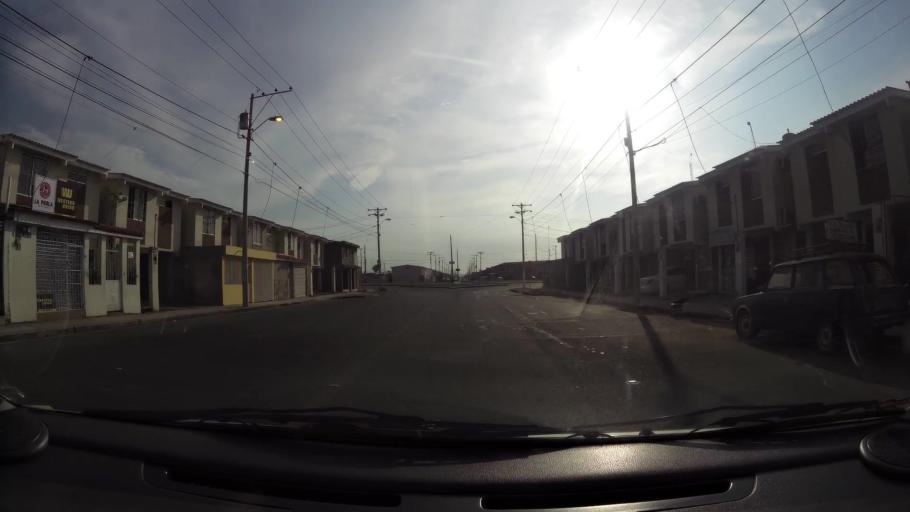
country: EC
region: Guayas
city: Eloy Alfaro
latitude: -2.0646
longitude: -79.8948
